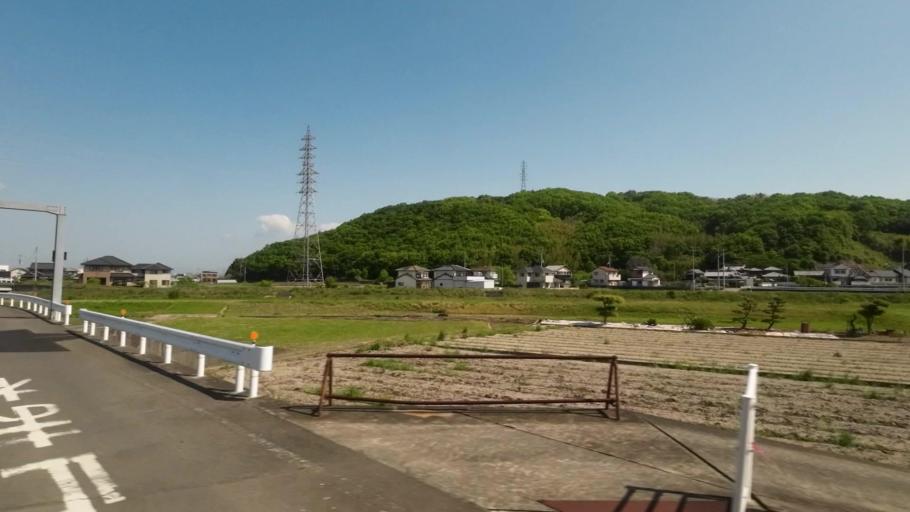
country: JP
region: Kagawa
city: Tadotsu
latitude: 34.2521
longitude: 133.7373
